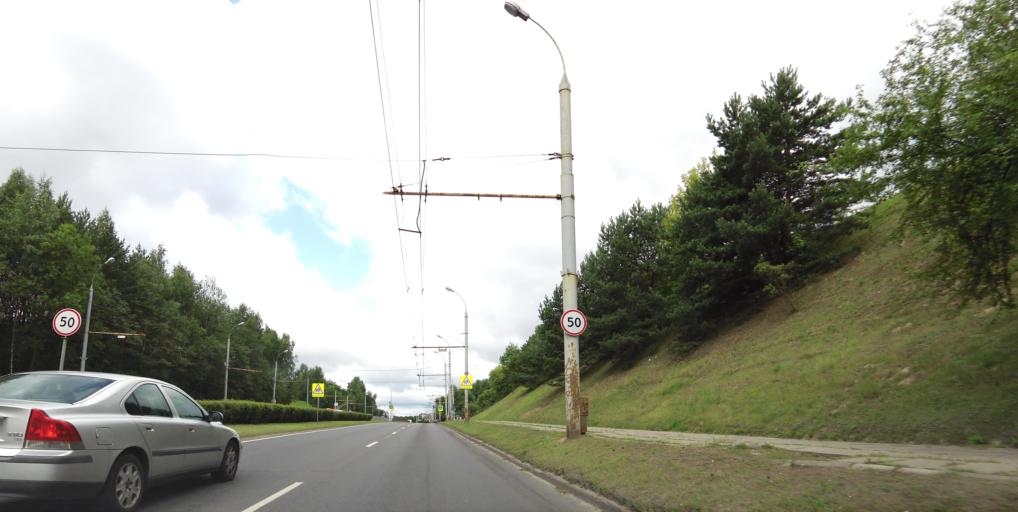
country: LT
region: Vilnius County
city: Seskine
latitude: 54.7005
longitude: 25.2323
